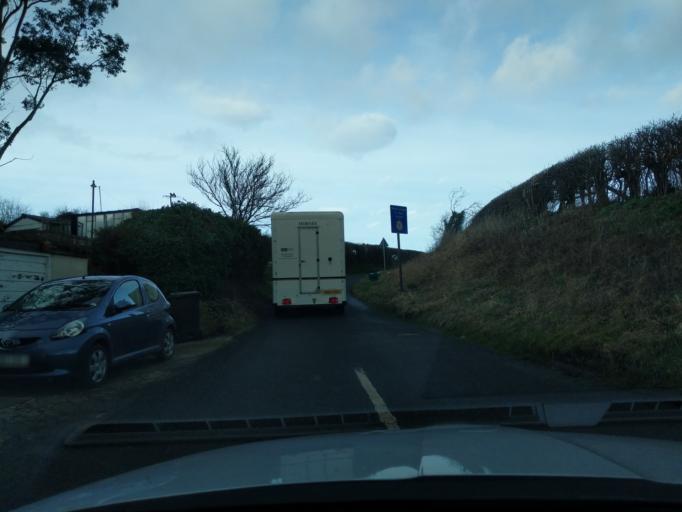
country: GB
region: England
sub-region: North Yorkshire
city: Catterick
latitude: 54.3604
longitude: -1.6631
